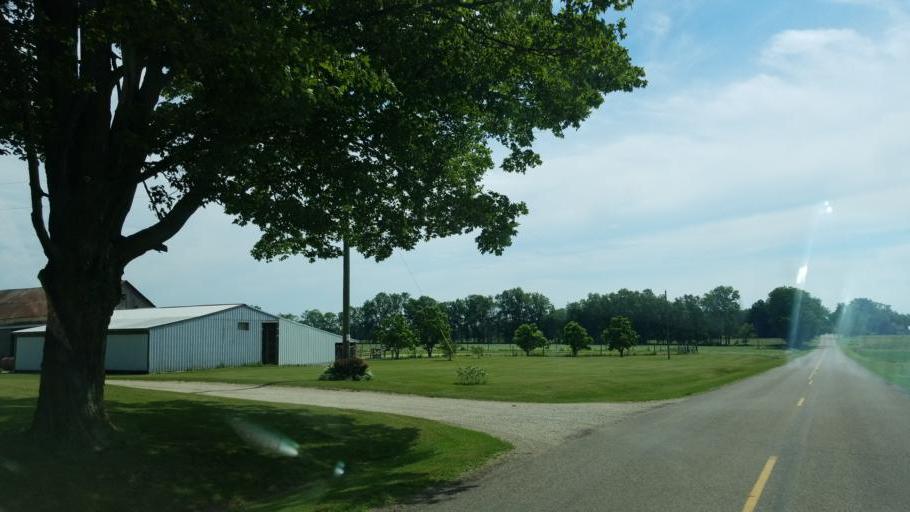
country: US
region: Michigan
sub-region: Barry County
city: Nashville
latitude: 42.6834
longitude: -85.0282
